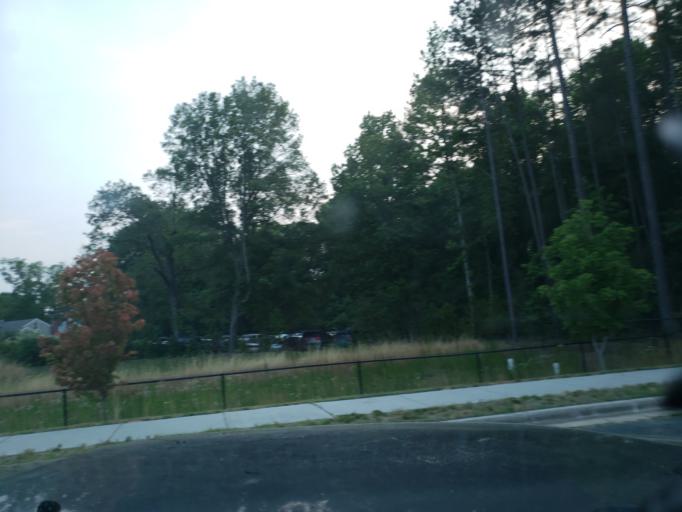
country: US
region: North Carolina
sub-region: Durham County
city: Gorman
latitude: 35.9879
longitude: -78.8440
